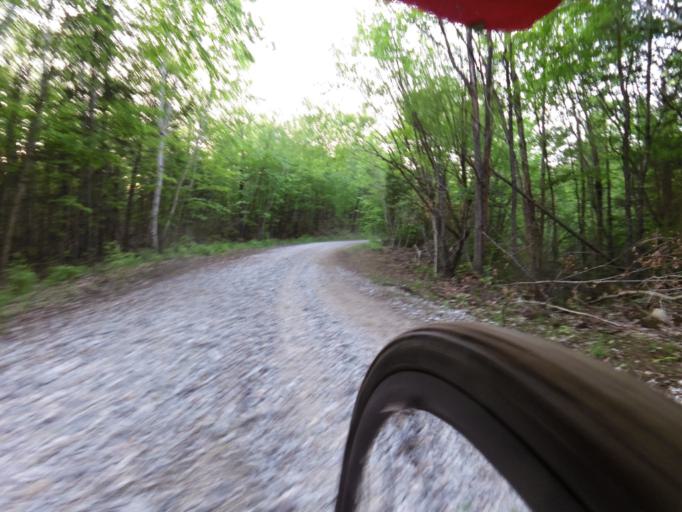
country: CA
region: Ontario
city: Arnprior
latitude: 45.1808
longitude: -76.5041
